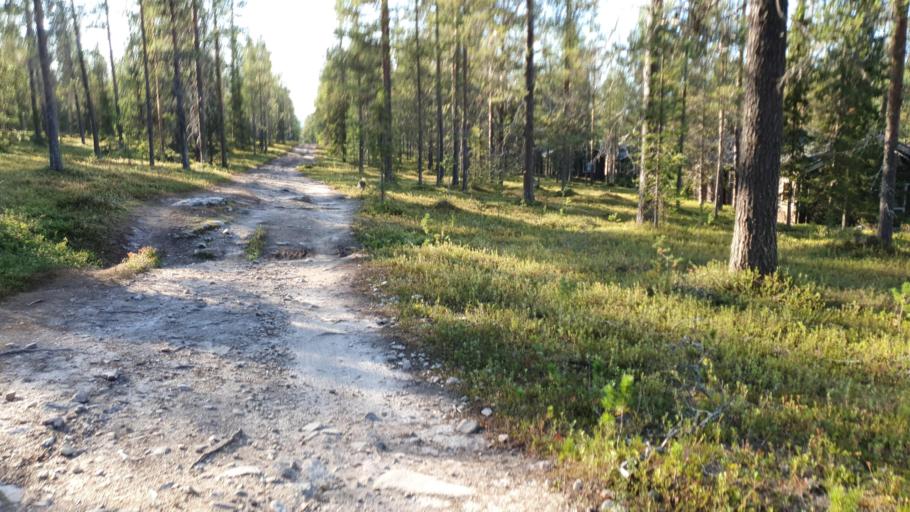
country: FI
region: Lapland
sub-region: Tunturi-Lappi
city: Kolari
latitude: 67.5984
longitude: 24.1955
